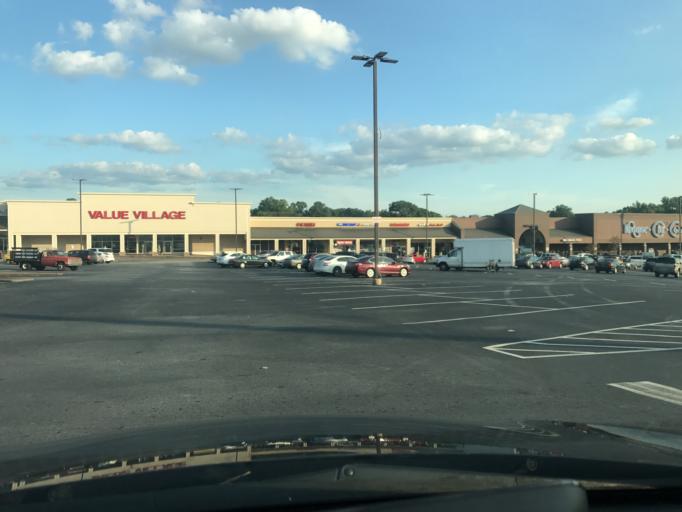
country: US
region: Georgia
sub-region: DeKalb County
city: Belvedere Park
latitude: 33.7535
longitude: -84.2694
